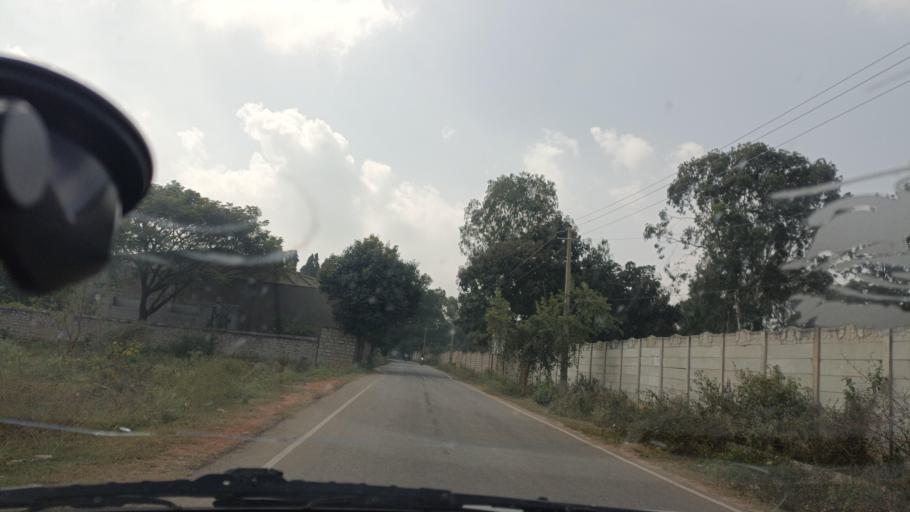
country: IN
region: Karnataka
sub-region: Bangalore Urban
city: Yelahanka
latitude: 13.1523
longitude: 77.6071
